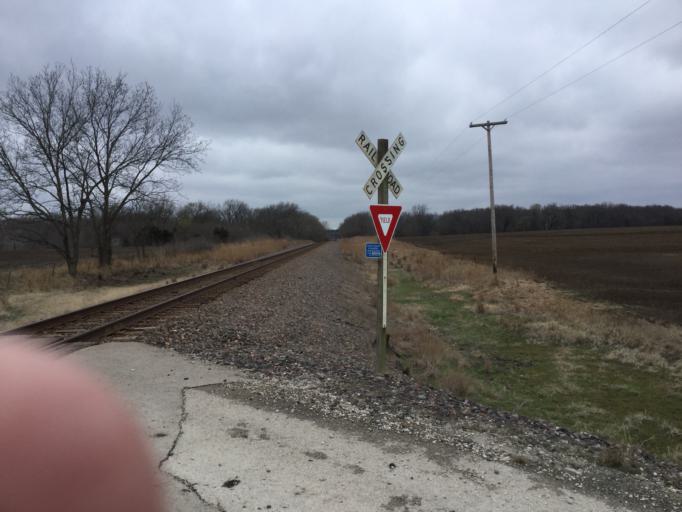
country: US
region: Kansas
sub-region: Wilson County
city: Fredonia
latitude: 37.5901
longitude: -95.7100
